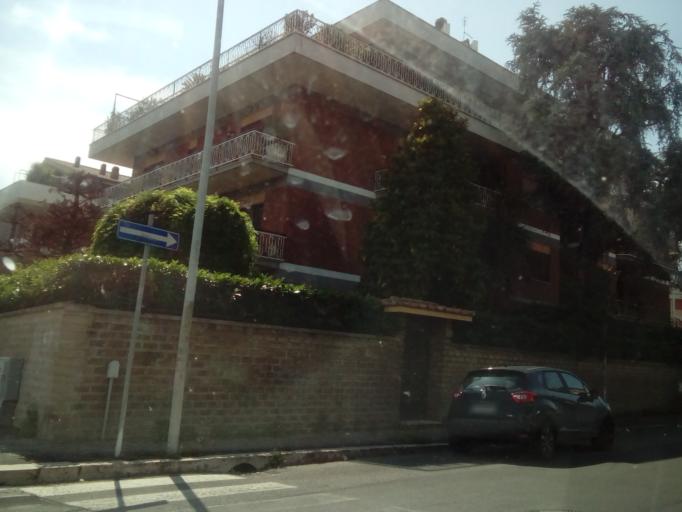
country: IT
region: Latium
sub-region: Citta metropolitana di Roma Capitale
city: Ciampino
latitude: 41.8494
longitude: 12.5655
